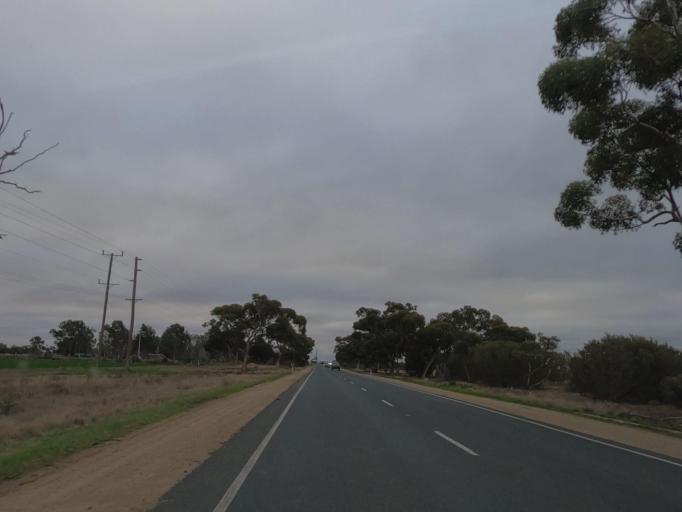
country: AU
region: Victoria
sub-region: Swan Hill
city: Swan Hill
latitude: -35.3985
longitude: 143.5753
